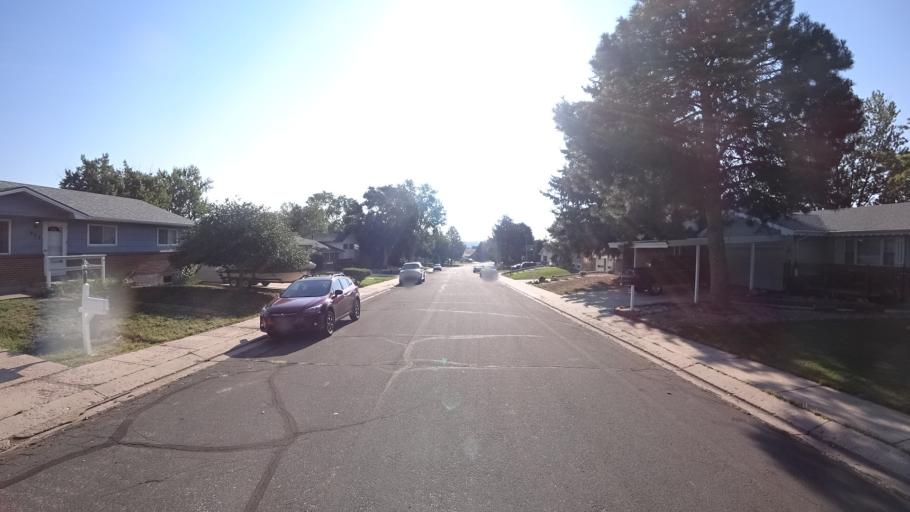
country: US
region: Colorado
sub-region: El Paso County
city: Colorado Springs
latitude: 38.8924
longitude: -104.8383
